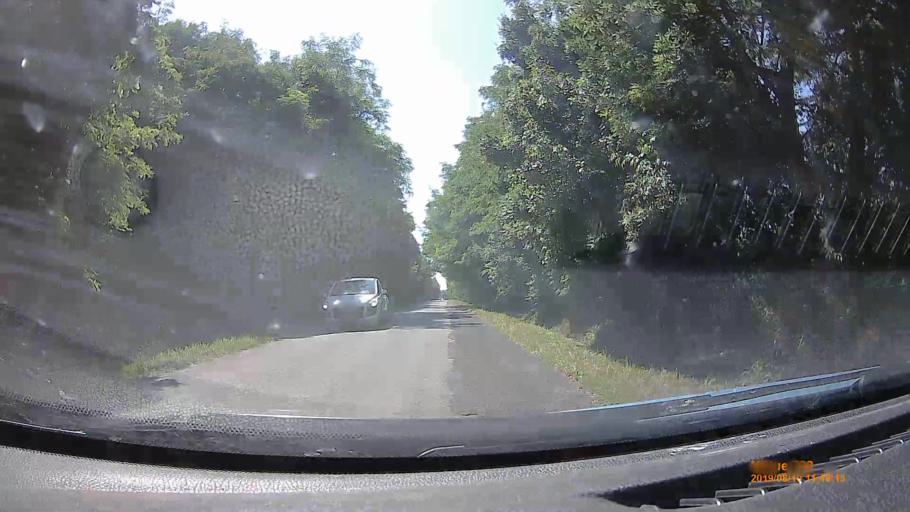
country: HU
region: Somogy
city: Somogyvar
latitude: 46.5061
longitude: 17.7350
